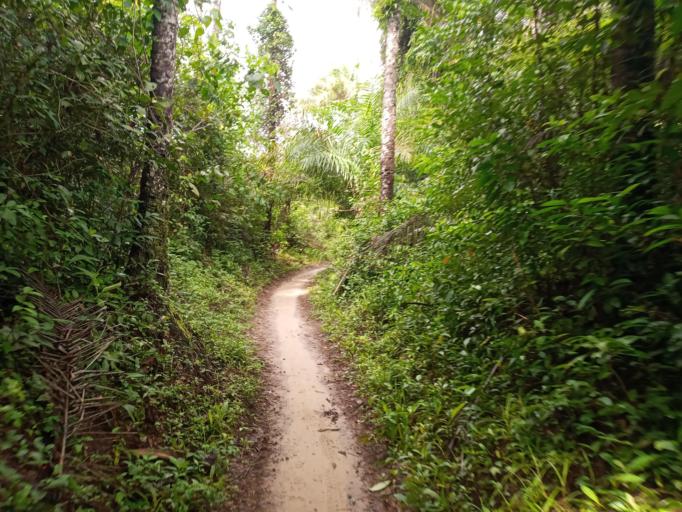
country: SL
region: Southern Province
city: Bonthe
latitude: 7.5148
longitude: -12.5467
